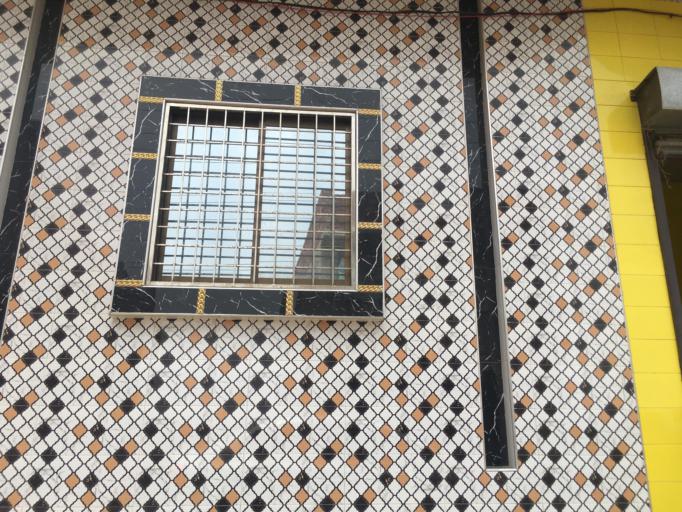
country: PK
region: Punjab
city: Lahore
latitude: 31.6126
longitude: 74.3544
